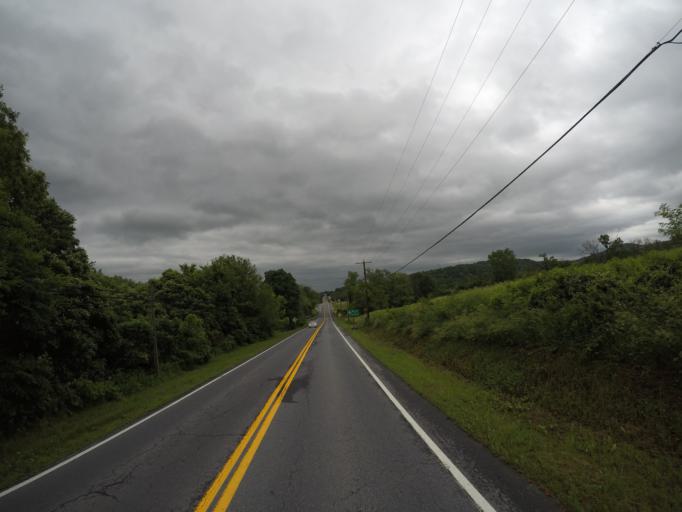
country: US
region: Maryland
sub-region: Washington County
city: Boonsboro
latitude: 39.4951
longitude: -77.6426
